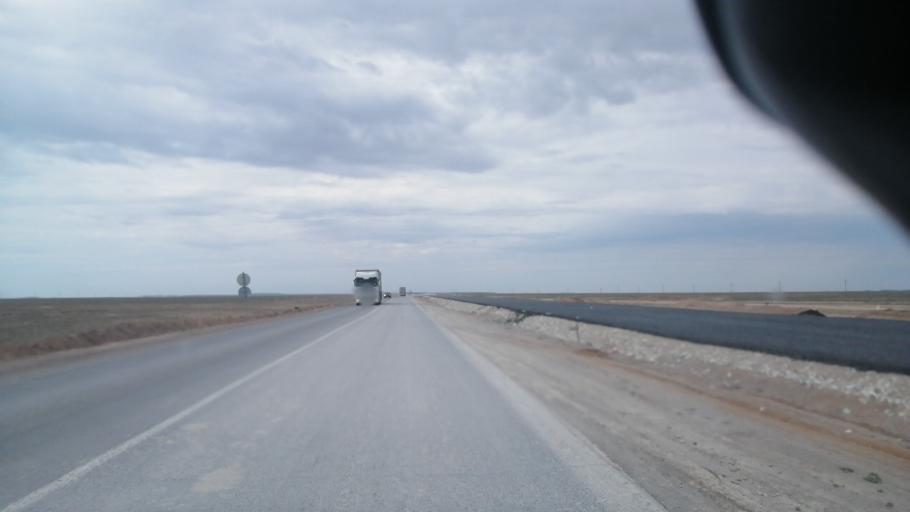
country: KZ
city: Priozersk
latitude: 46.5437
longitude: 74.1679
